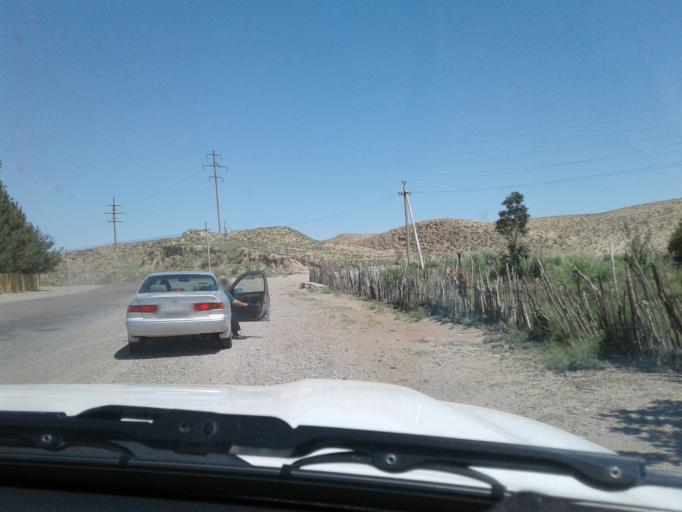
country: AF
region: Badghis
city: Bala Murghab
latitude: 35.9522
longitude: 62.9056
